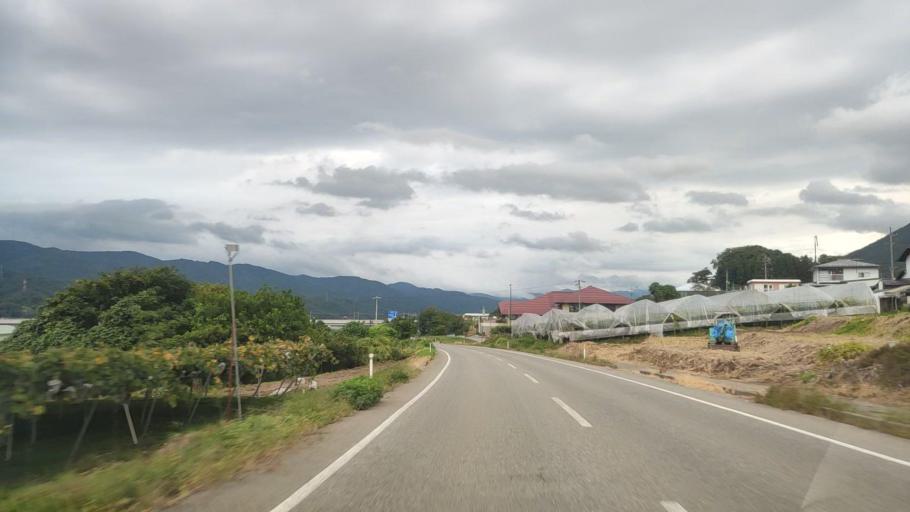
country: JP
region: Nagano
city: Nakano
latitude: 36.7842
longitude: 138.3627
